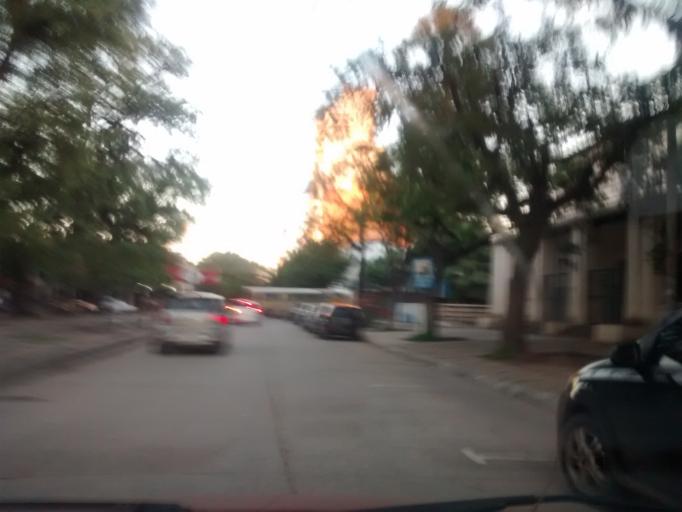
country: AR
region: Chaco
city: Resistencia
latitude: -27.4516
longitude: -58.9938
